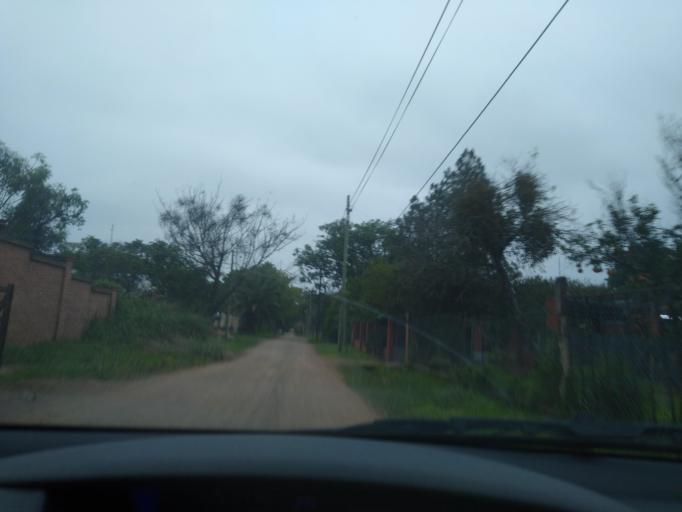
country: AR
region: Chaco
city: Colonia Benitez
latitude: -27.3297
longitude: -58.9536
